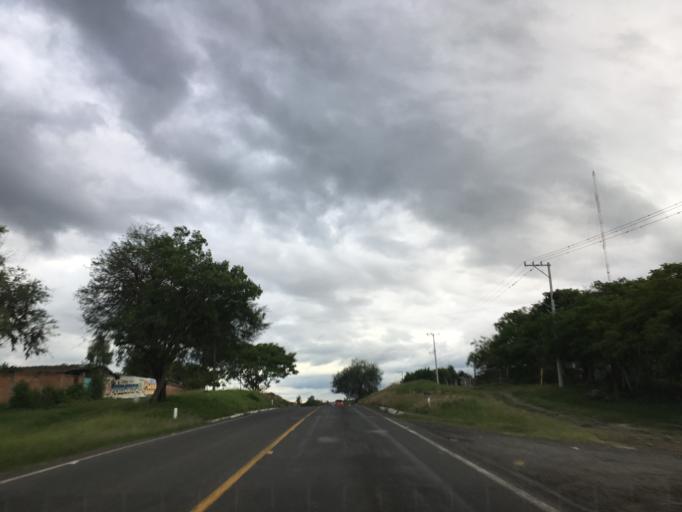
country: MX
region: Michoacan
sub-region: Cuitzeo
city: Cuamio
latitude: 20.0300
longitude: -101.1529
